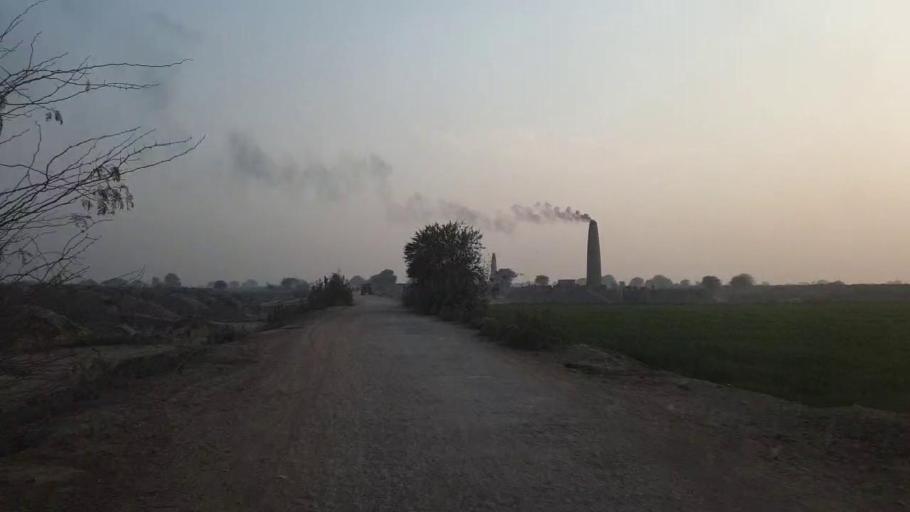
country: PK
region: Sindh
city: Bhit Shah
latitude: 25.7801
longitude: 68.4626
